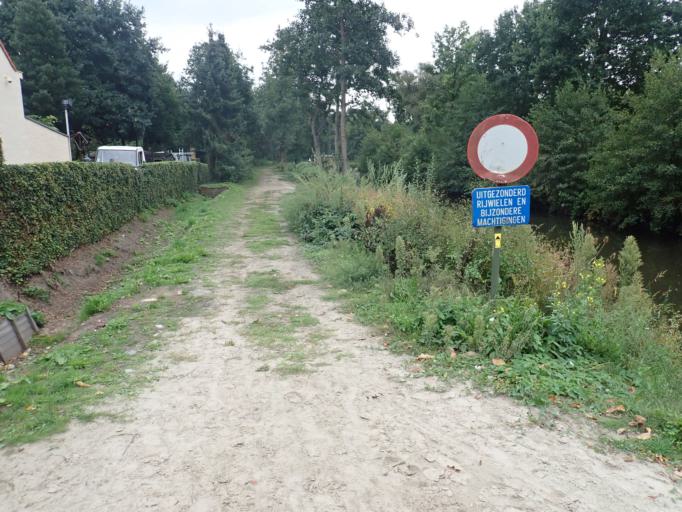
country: BE
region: Flanders
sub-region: Provincie Antwerpen
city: Brasschaat
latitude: 51.3237
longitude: 4.5028
